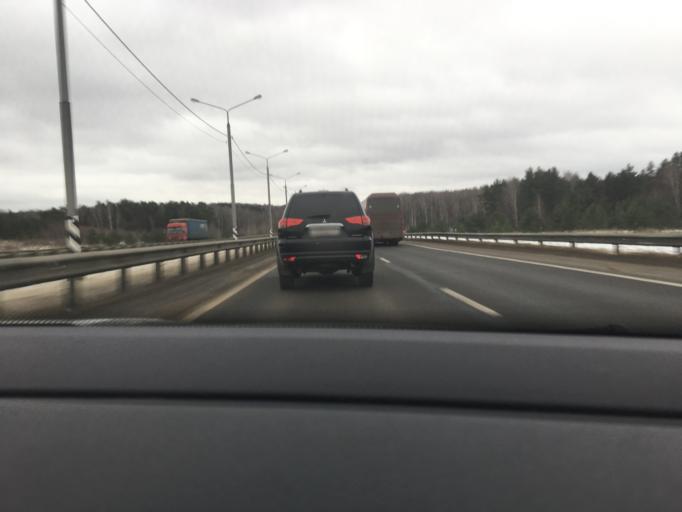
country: RU
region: Tula
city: Zaokskiy
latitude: 54.8220
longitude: 37.4724
